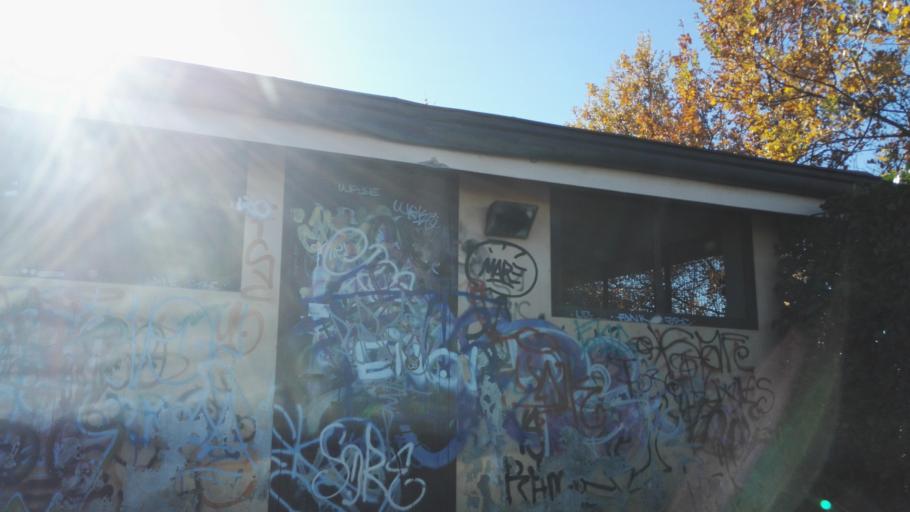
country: IT
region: Lombardy
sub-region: Citta metropolitana di Milano
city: Poasco-Sorigherio
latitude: 45.3969
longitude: 9.2380
